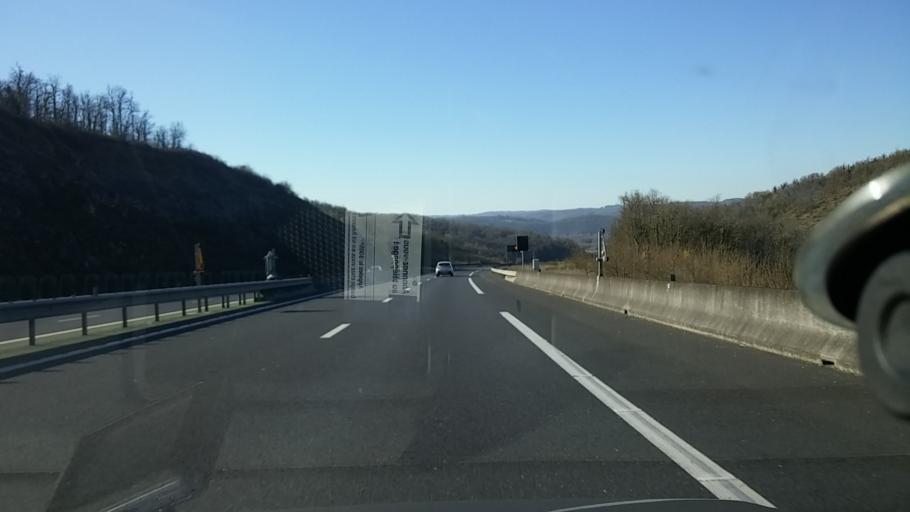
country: FR
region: Midi-Pyrenees
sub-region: Departement du Lot
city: Souillac
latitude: 44.8740
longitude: 1.5071
